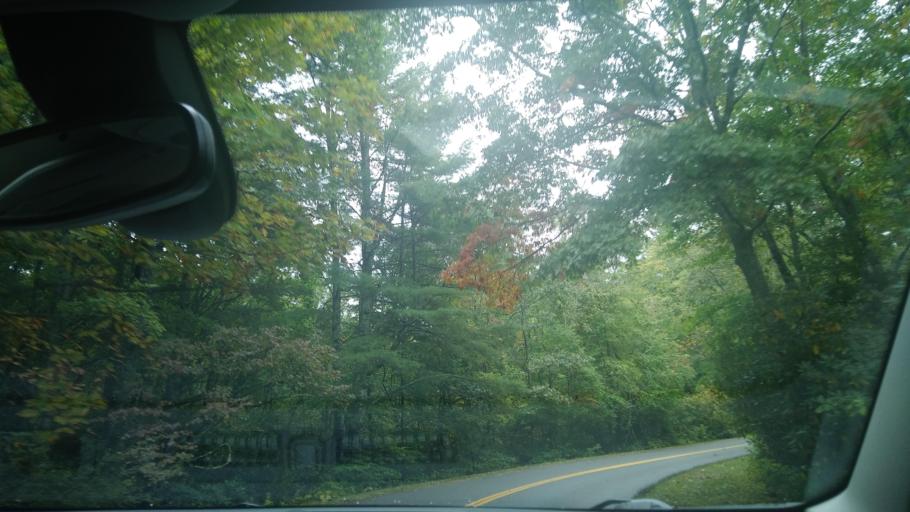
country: US
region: North Carolina
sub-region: Mitchell County
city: Spruce Pine
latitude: 35.9103
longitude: -81.9689
